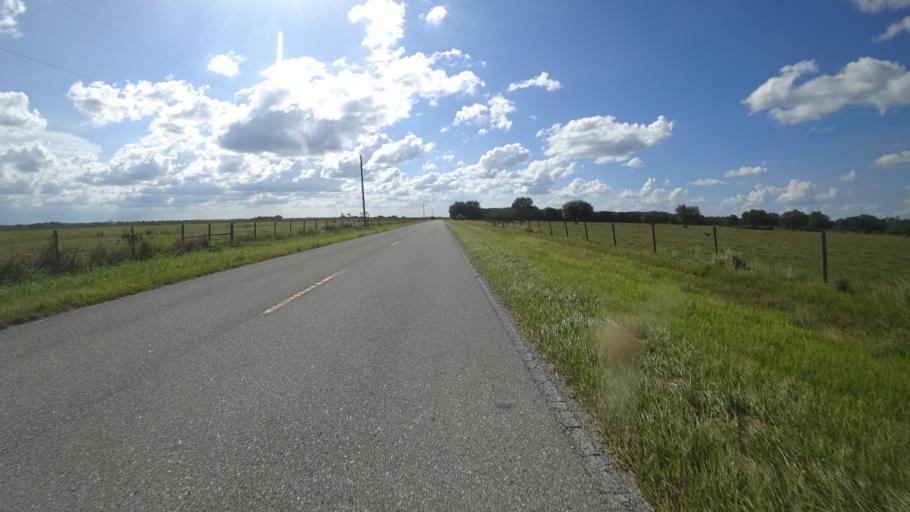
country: US
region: Florida
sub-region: DeSoto County
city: Nocatee
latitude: 27.2700
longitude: -82.0840
